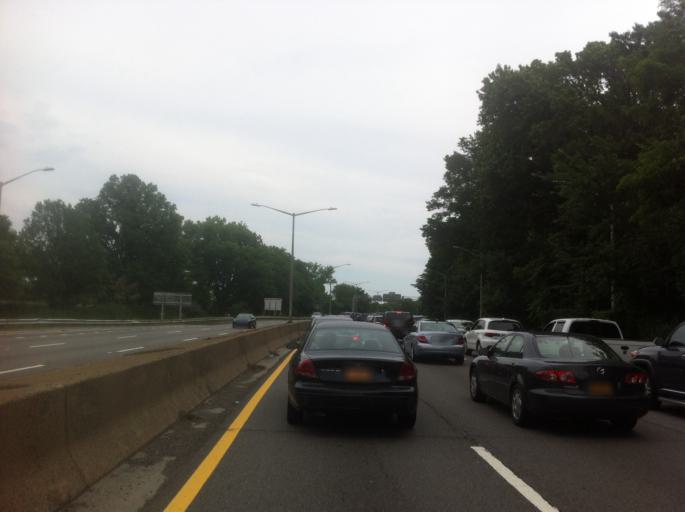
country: US
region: New York
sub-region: Nassau County
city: East Atlantic Beach
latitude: 40.7888
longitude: -73.7794
